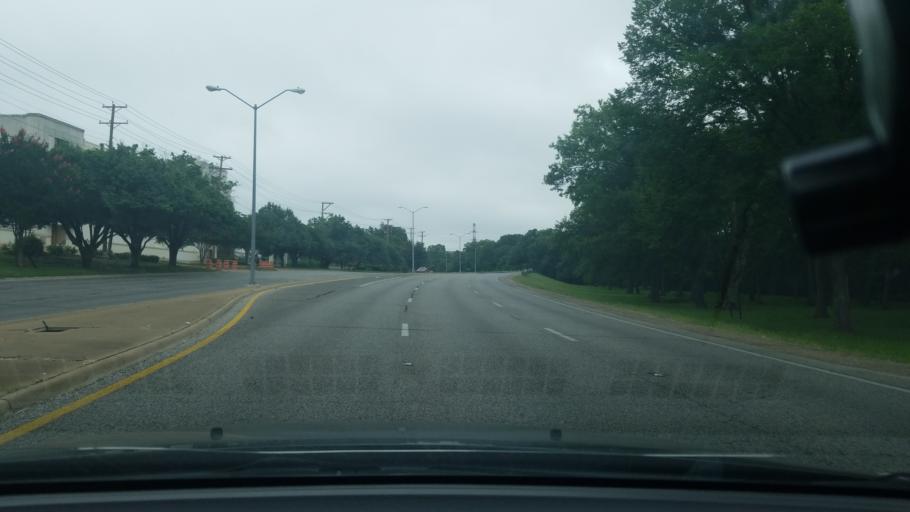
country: US
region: Texas
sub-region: Dallas County
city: Balch Springs
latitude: 32.7633
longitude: -96.6935
